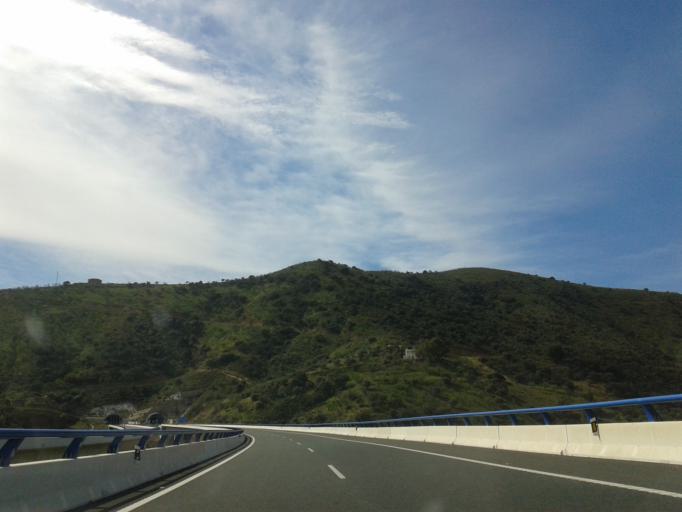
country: ES
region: Andalusia
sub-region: Provincia de Malaga
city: Casabermeja
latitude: 36.8753
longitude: -4.4823
